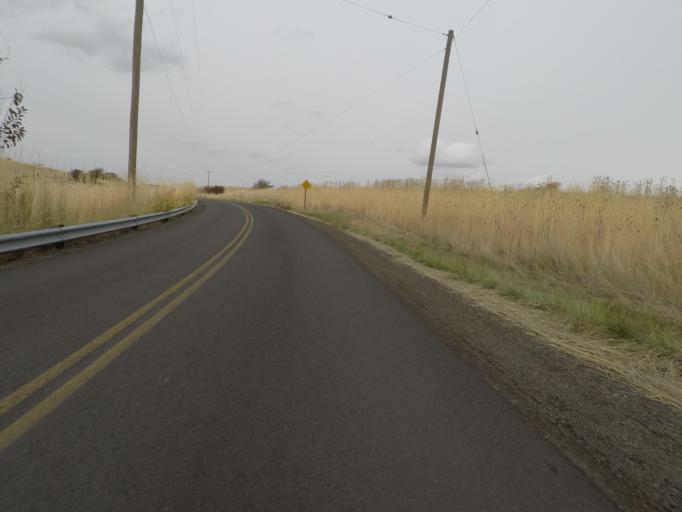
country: US
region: Washington
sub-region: Walla Walla County
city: Walla Walla East
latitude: 46.0720
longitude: -118.2700
